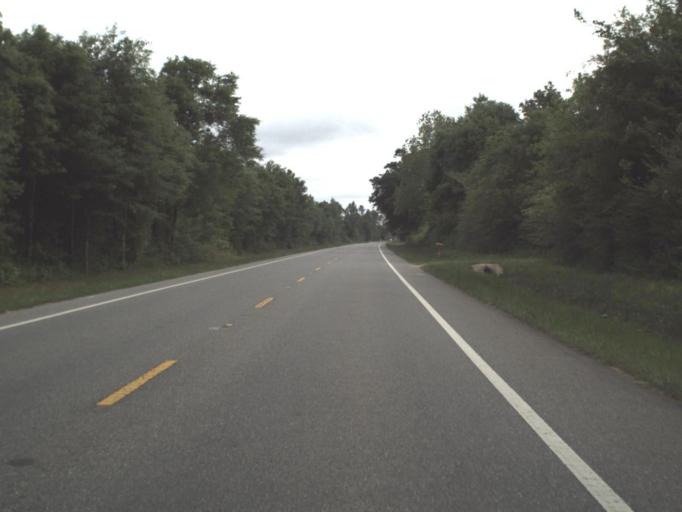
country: US
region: Florida
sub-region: Santa Rosa County
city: Point Baker
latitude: 30.7435
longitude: -87.0428
